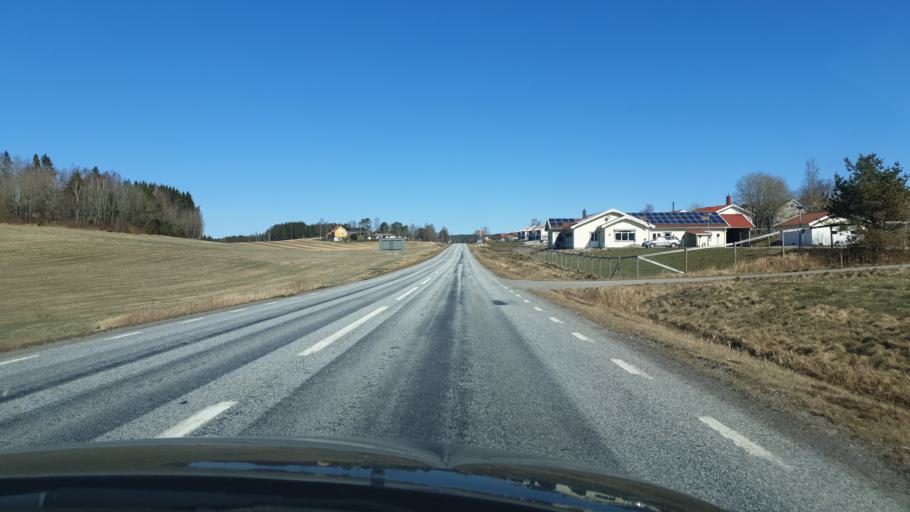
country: SE
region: Vaestra Goetaland
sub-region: Tanums Kommun
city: Tanumshede
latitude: 58.7717
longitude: 11.5572
